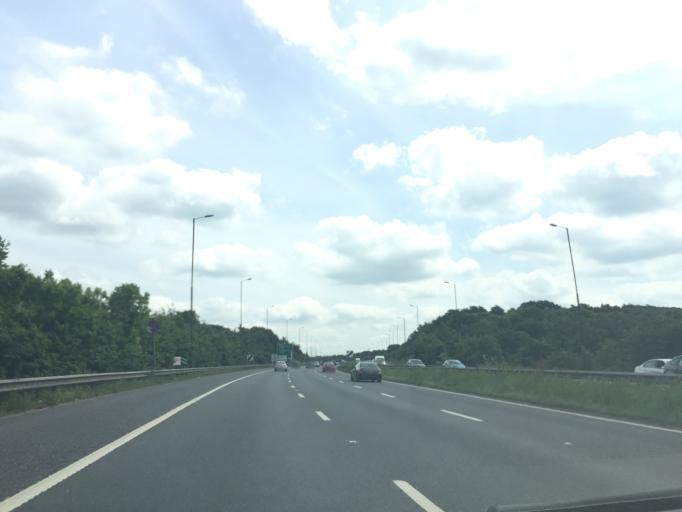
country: GB
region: England
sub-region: Greater London
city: Bexley
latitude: 51.4419
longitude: 0.1700
